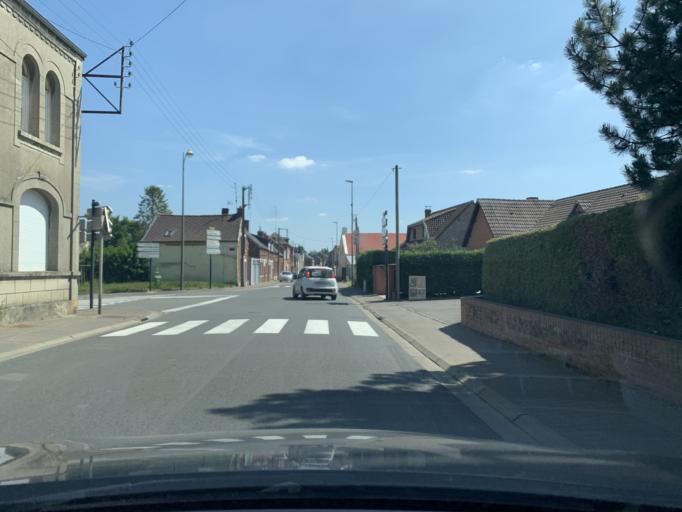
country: FR
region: Nord-Pas-de-Calais
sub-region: Departement du Nord
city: Caudry
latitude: 50.1236
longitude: 3.4007
